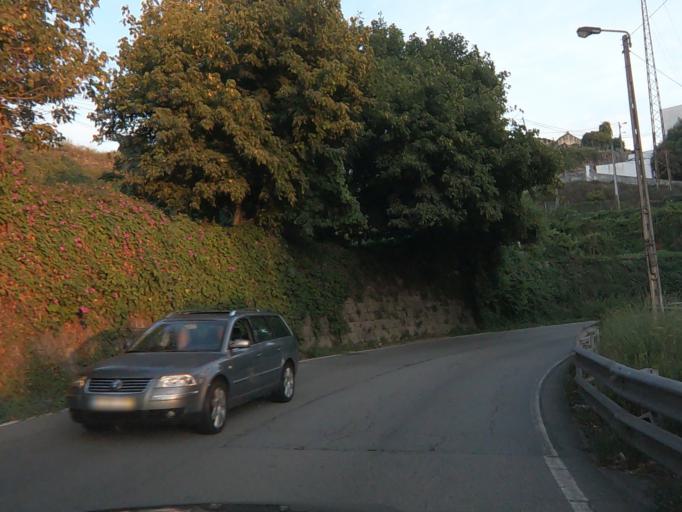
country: PT
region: Porto
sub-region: Gondomar
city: Valbom
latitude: 41.1411
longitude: -8.5721
